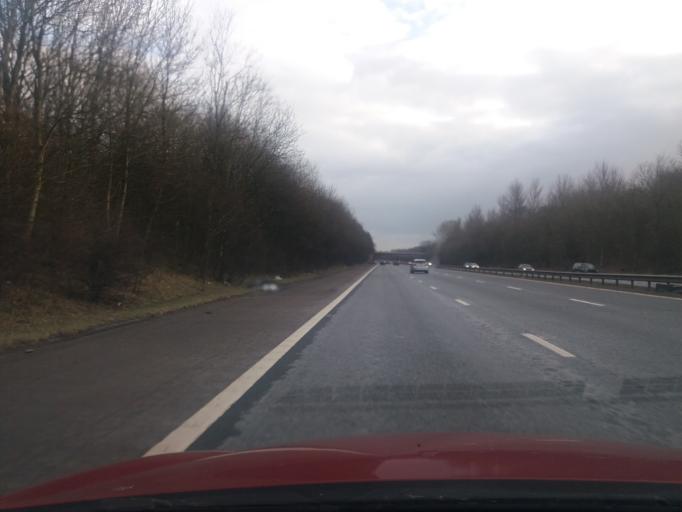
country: GB
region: England
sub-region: Lancashire
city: Clayton-le-Woods
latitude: 53.7079
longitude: -2.6314
